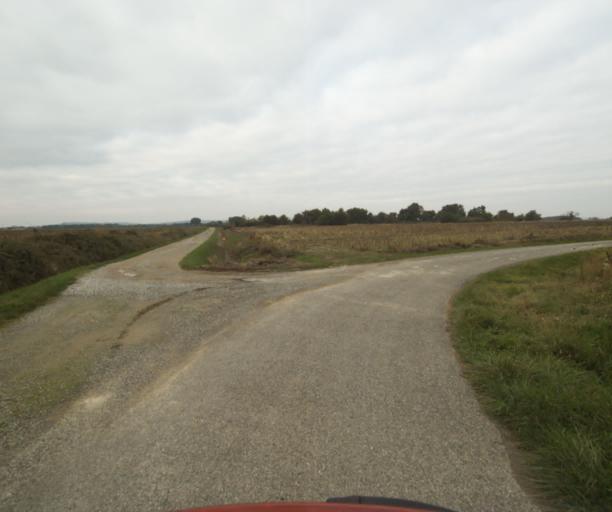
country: FR
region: Midi-Pyrenees
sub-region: Departement de la Haute-Garonne
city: Launac
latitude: 43.8012
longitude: 1.1937
